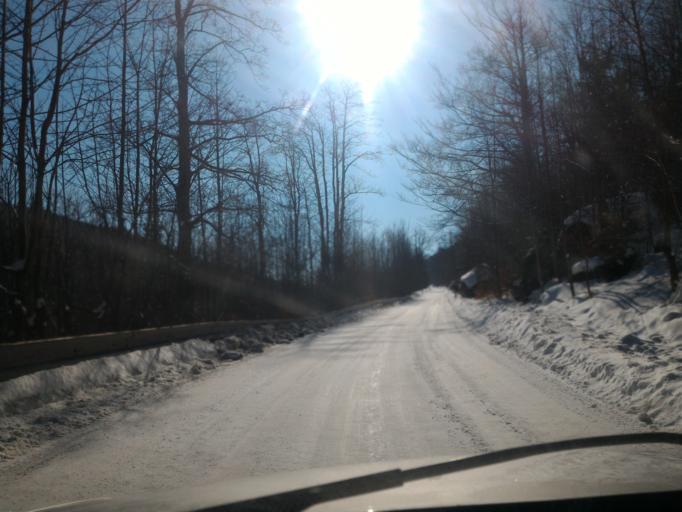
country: CZ
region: Liberecky
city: Nove Mesto pod Smrkem
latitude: 50.8563
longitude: 15.2585
